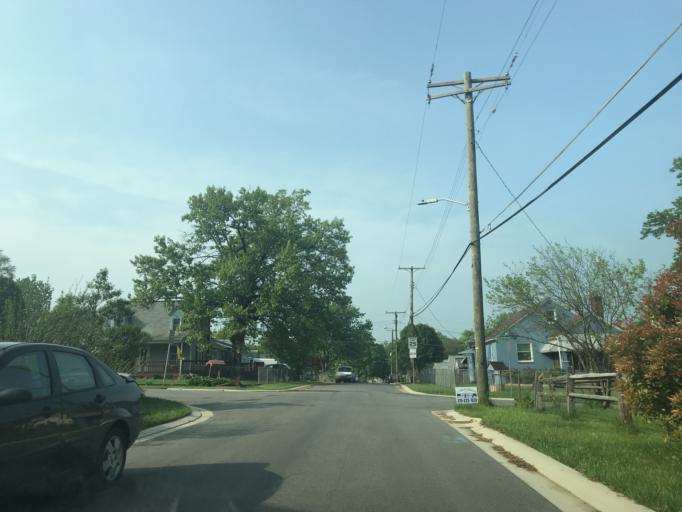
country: US
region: Maryland
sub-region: Baltimore County
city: Parkville
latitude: 39.3832
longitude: -76.5607
